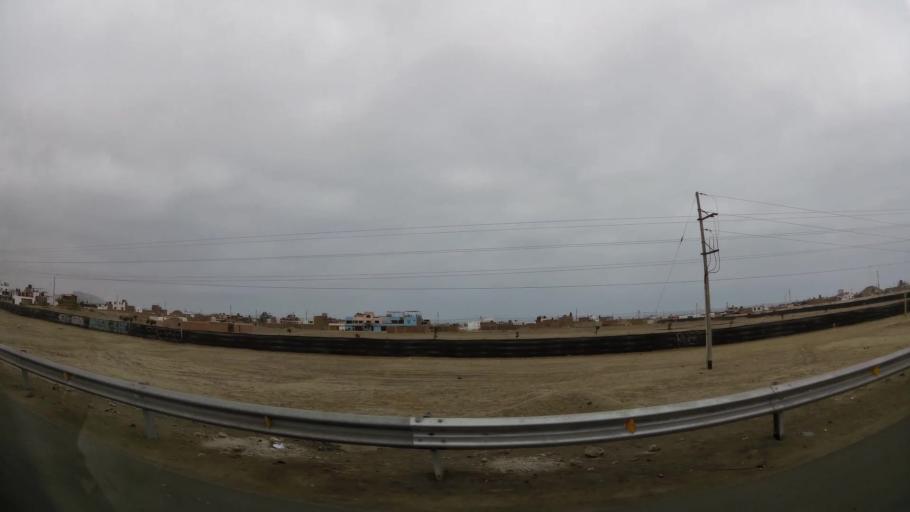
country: PE
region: Lima
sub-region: Lima
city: San Bartolo
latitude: -12.3689
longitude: -76.7873
